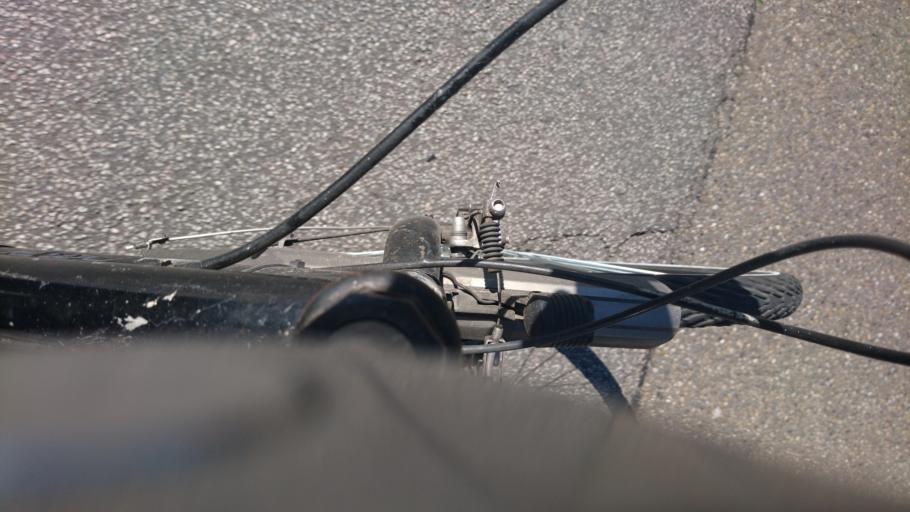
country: DE
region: Baden-Wuerttemberg
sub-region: Karlsruhe Region
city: Mannheim
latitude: 49.4723
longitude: 8.4900
